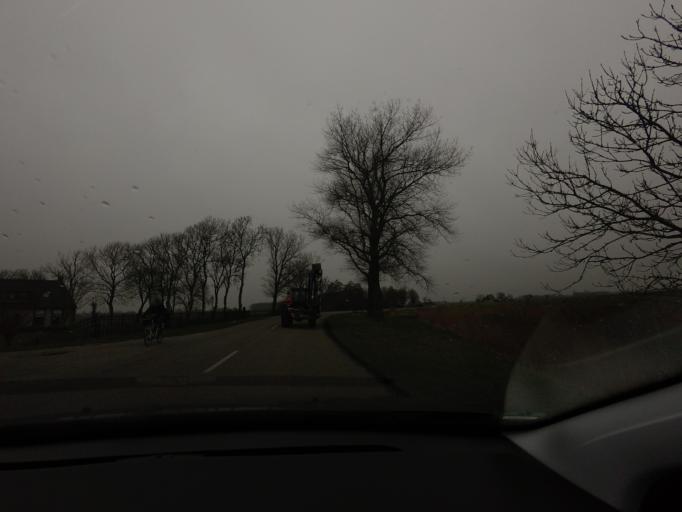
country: NL
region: Friesland
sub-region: Gemeente Franekeradeel
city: Franeker
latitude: 53.1717
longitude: 5.5444
